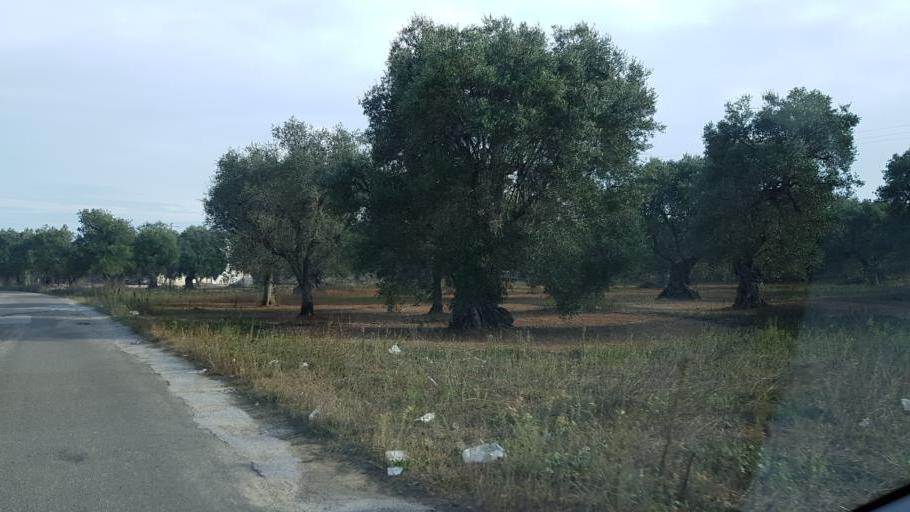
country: IT
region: Apulia
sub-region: Provincia di Brindisi
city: Oria
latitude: 40.4994
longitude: 17.6574
